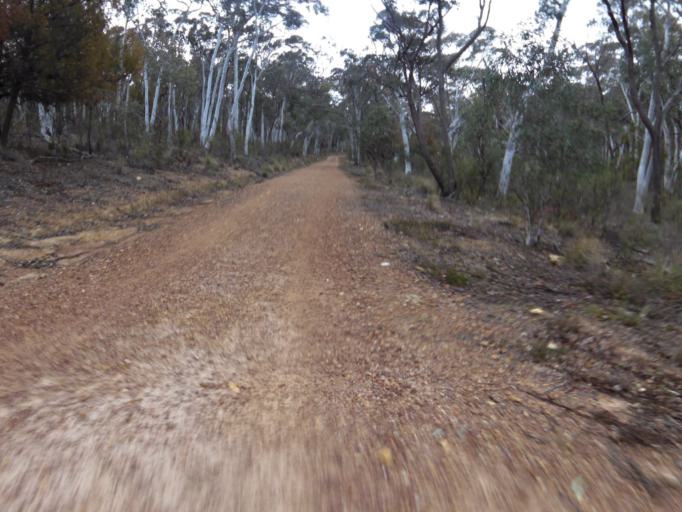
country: AU
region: Australian Capital Territory
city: Acton
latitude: -35.2652
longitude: 149.0946
